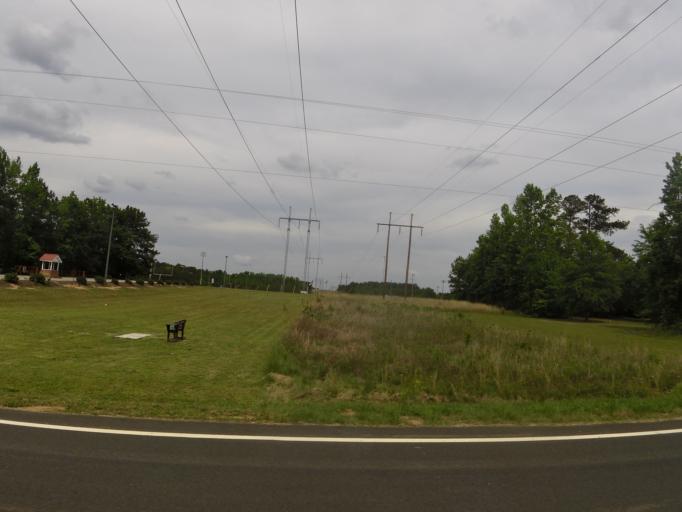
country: US
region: Georgia
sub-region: McDuffie County
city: Thomson
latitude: 33.4302
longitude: -82.4875
